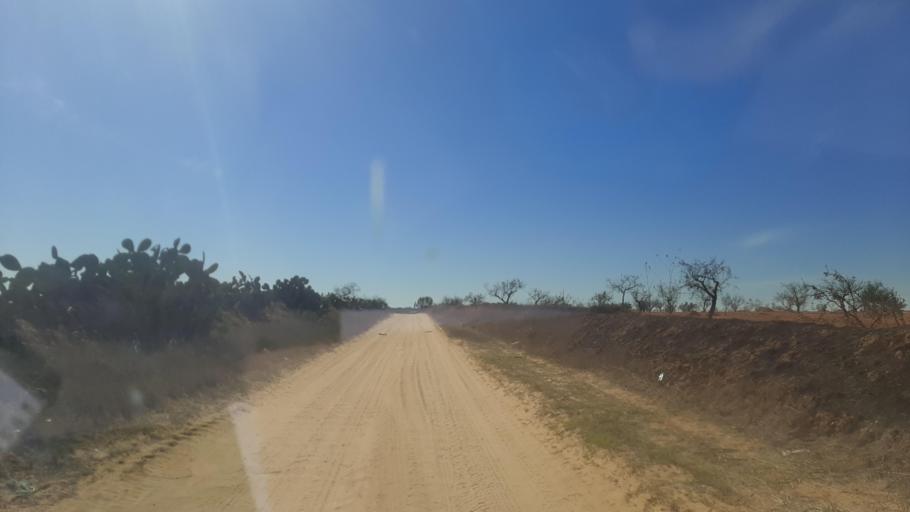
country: TN
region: Safaqis
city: Sfax
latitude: 34.8367
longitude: 10.5582
